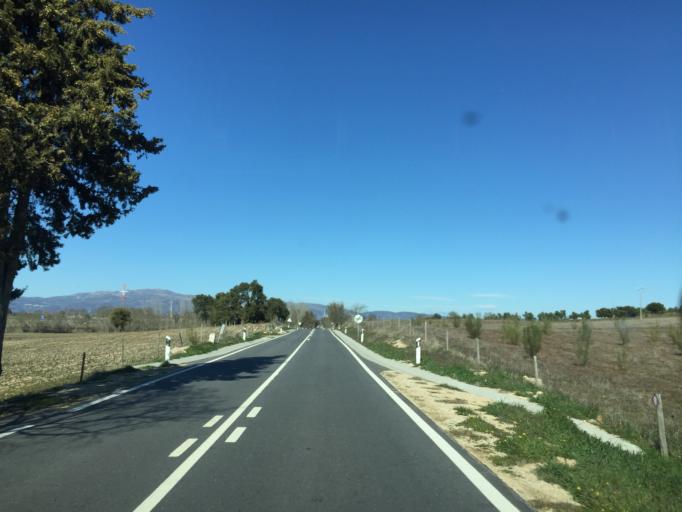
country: PT
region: Guarda
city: Alcains
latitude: 39.9652
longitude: -7.4535
